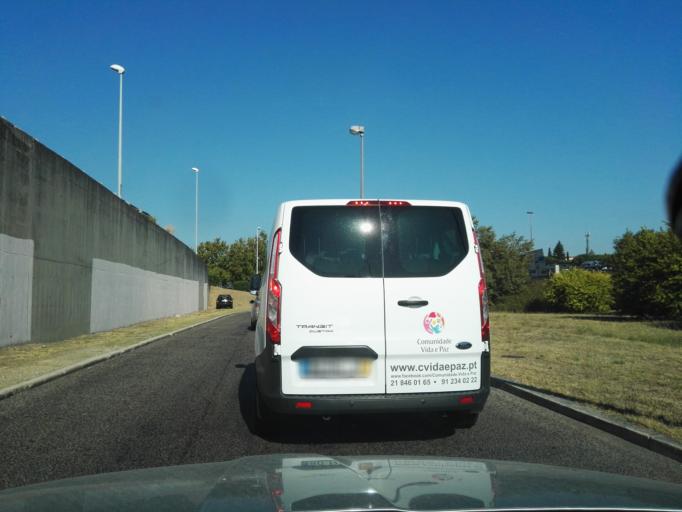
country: PT
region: Lisbon
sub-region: Loures
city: Moscavide
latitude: 38.7642
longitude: -9.1307
